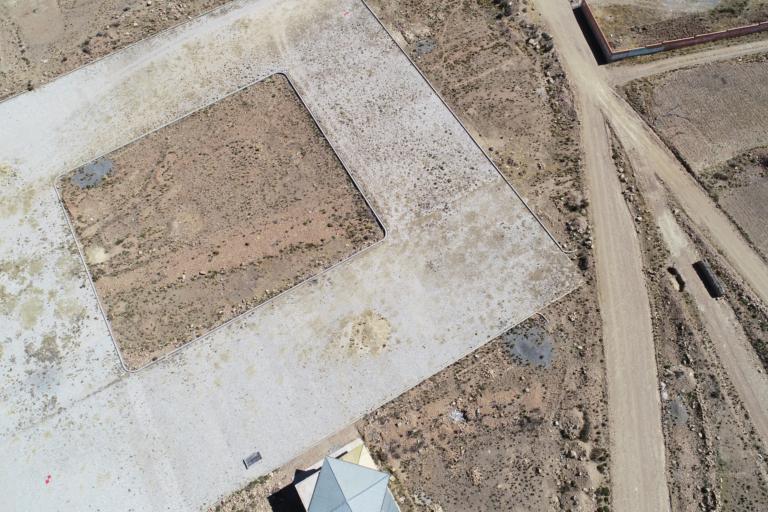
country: BO
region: La Paz
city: Achacachi
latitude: -15.8869
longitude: -68.8116
